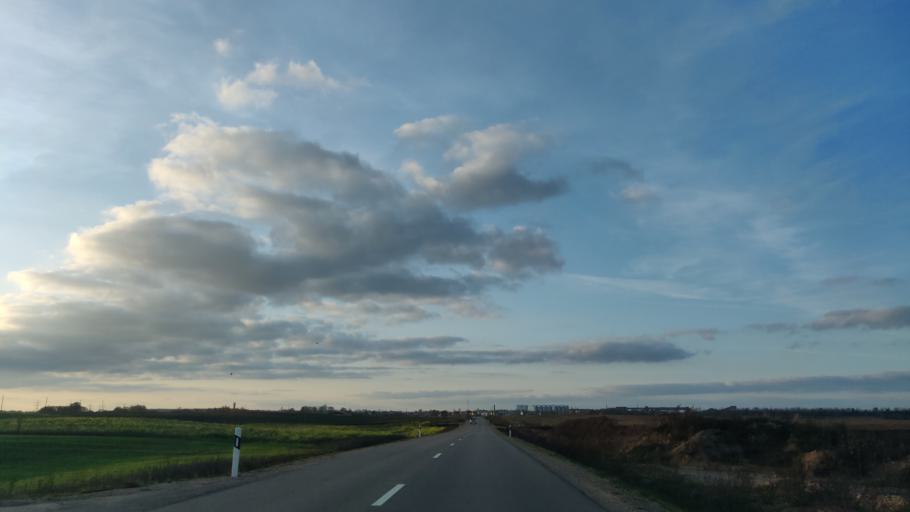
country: LT
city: Lentvaris
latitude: 54.6034
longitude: 25.0044
